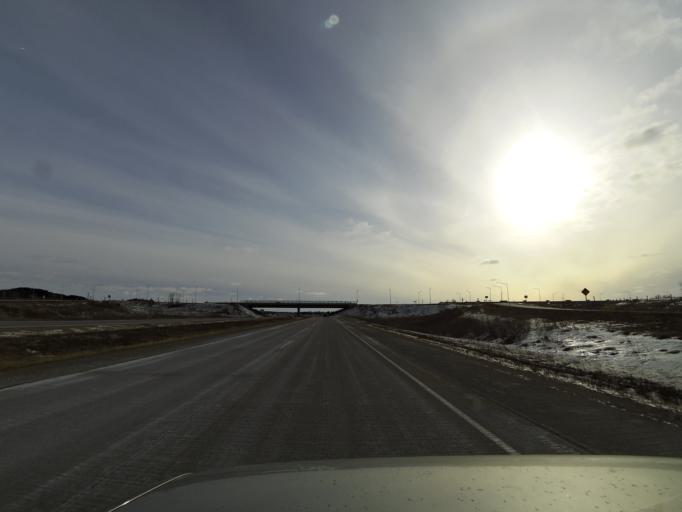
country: US
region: Wisconsin
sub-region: Saint Croix County
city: Hudson
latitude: 44.9511
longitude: -92.6954
